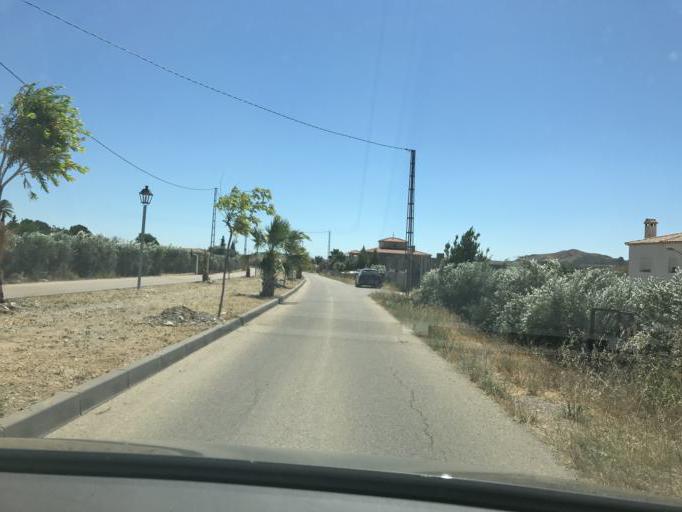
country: ES
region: Andalusia
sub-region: Provincia de Almeria
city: Fines
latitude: 37.3559
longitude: -2.2562
